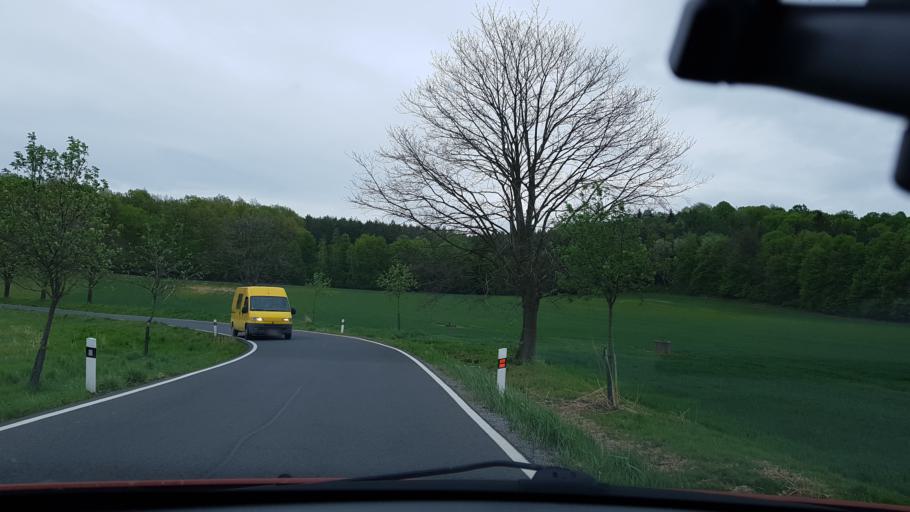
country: CZ
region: Olomoucky
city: Vidnava
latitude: 50.3858
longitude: 17.1222
